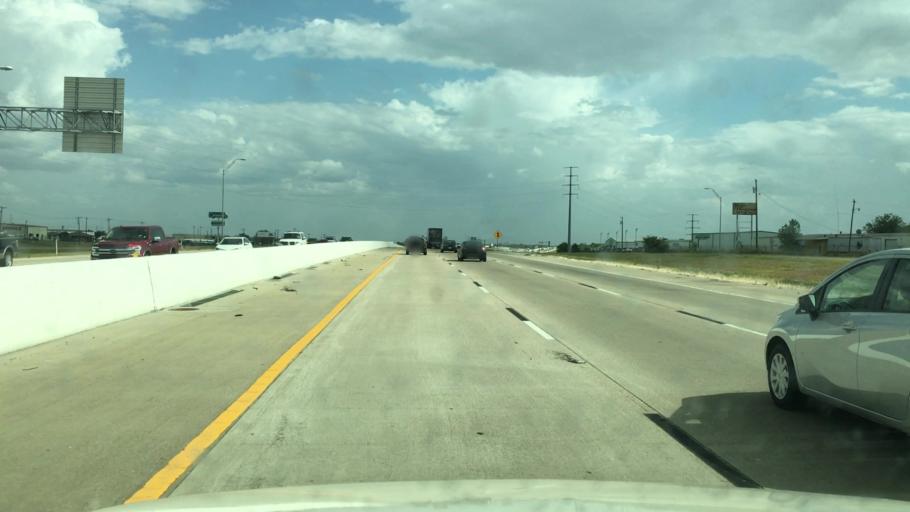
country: US
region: Texas
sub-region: McLennan County
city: Northcrest
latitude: 31.6972
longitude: -97.1016
